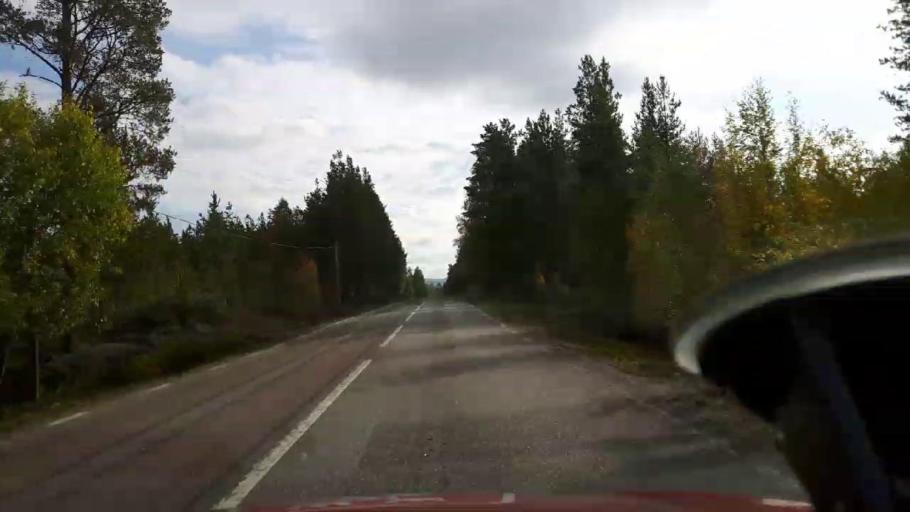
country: SE
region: Jaemtland
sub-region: Harjedalens Kommun
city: Sveg
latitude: 62.1243
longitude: 14.9951
